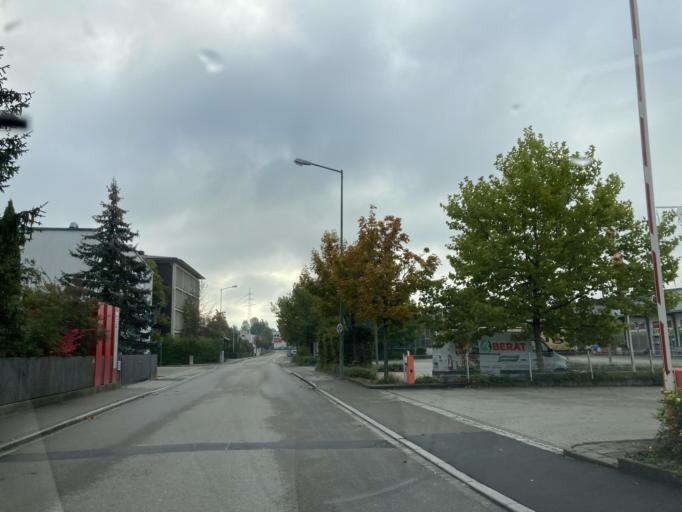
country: DE
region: Bavaria
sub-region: Swabia
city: Augsburg
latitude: 48.3462
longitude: 10.8823
